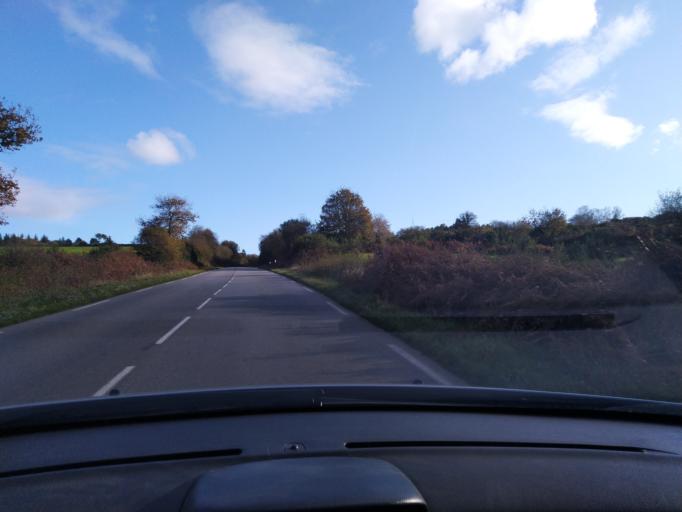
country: FR
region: Brittany
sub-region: Departement du Finistere
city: Guerlesquin
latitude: 48.5628
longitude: -3.6029
